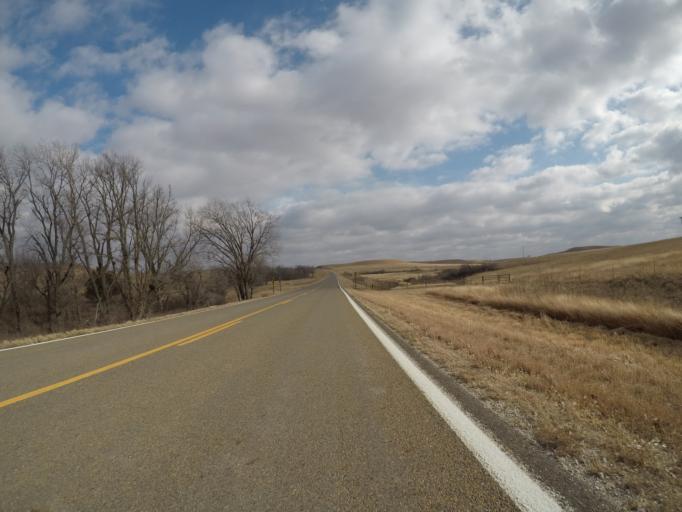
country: US
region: Kansas
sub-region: Wabaunsee County
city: Alma
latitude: 38.8710
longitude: -96.3496
